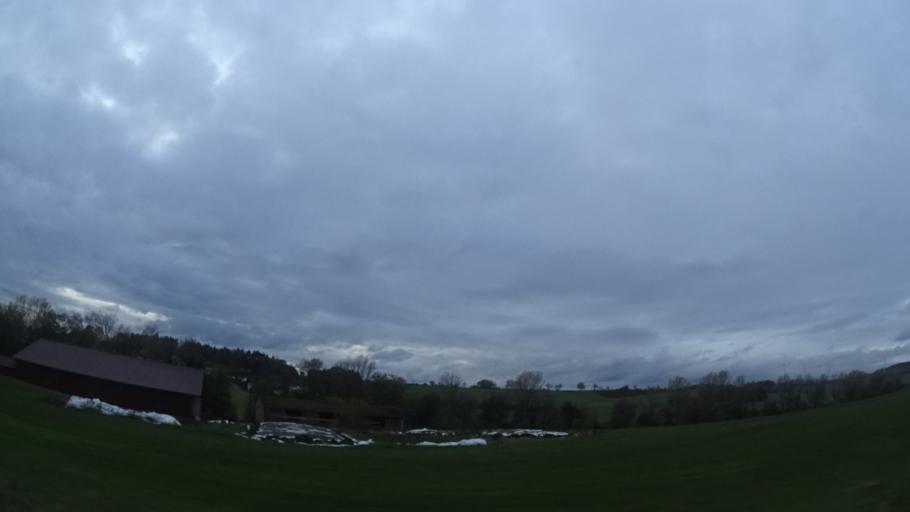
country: DE
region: Hesse
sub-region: Regierungsbezirk Giessen
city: Freiensteinau
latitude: 50.3756
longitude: 9.4273
